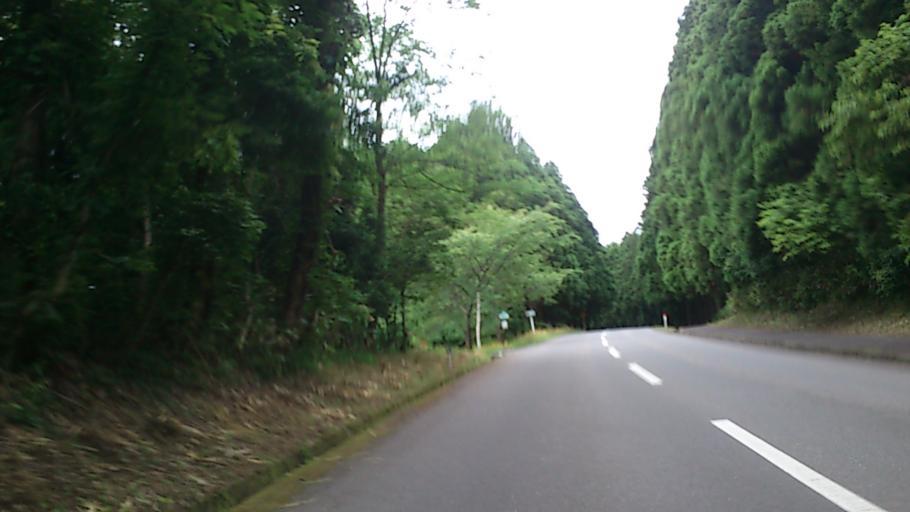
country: JP
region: Yamagata
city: Yuza
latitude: 39.0822
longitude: 139.8861
